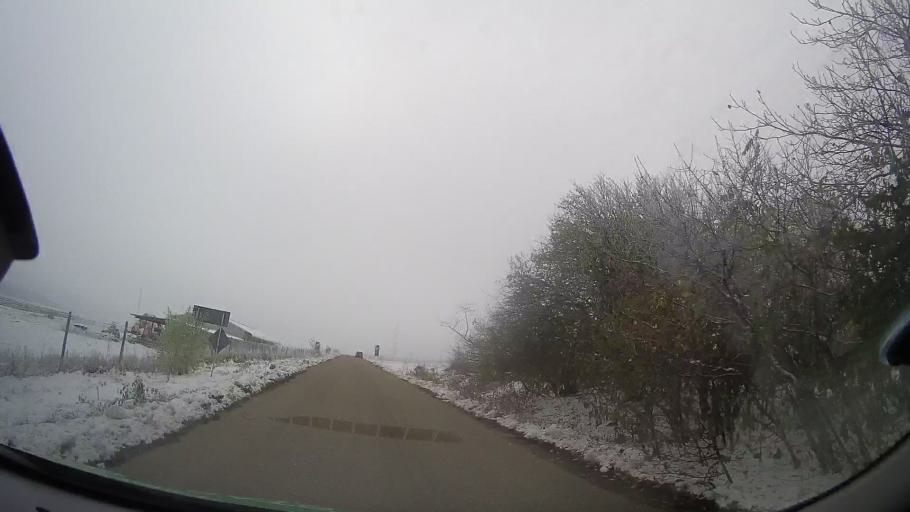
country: RO
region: Vaslui
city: Coroiesti
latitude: 46.2427
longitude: 27.4798
